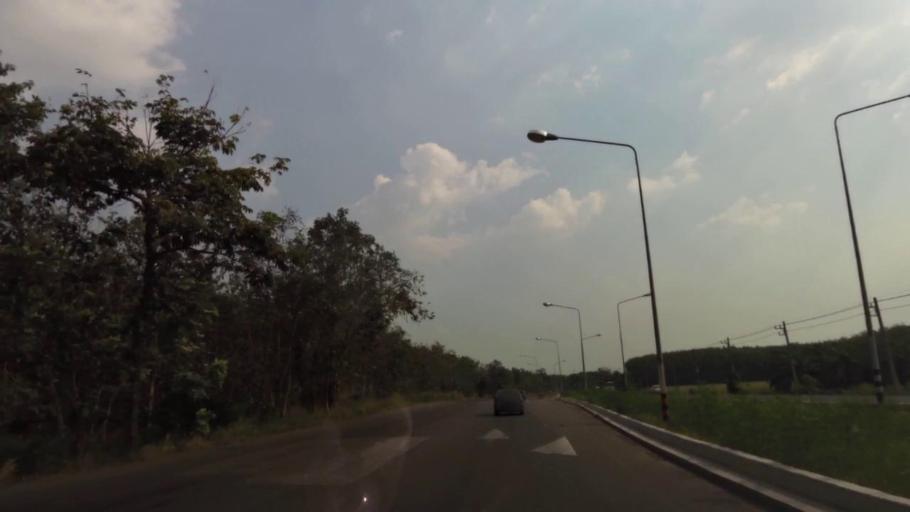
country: TH
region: Rayong
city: Wang Chan
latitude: 13.0095
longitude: 101.4791
